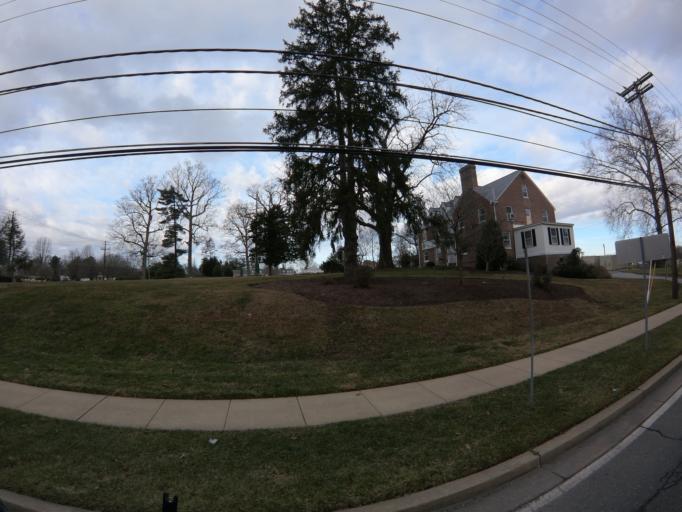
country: US
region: Maryland
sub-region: Montgomery County
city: Olney
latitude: 39.1502
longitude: -77.0577
